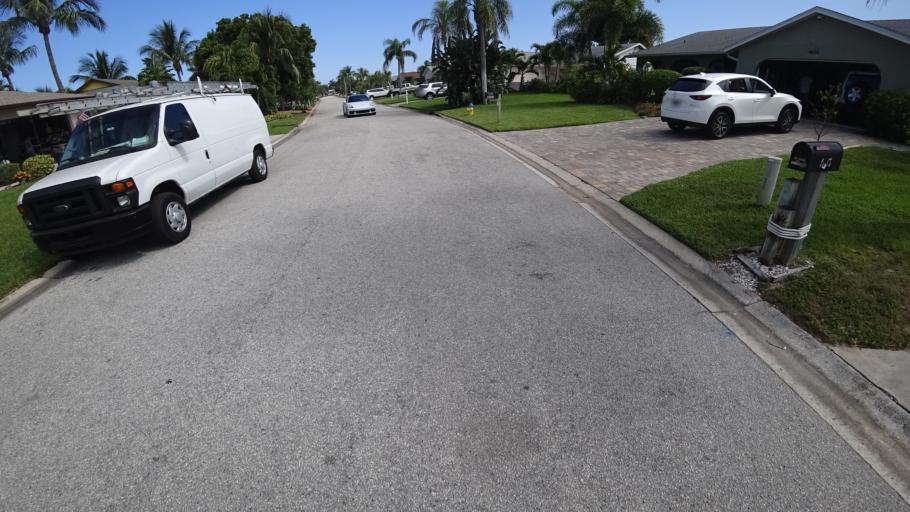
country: US
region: Florida
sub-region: Manatee County
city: Cortez
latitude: 27.4582
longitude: -82.6527
